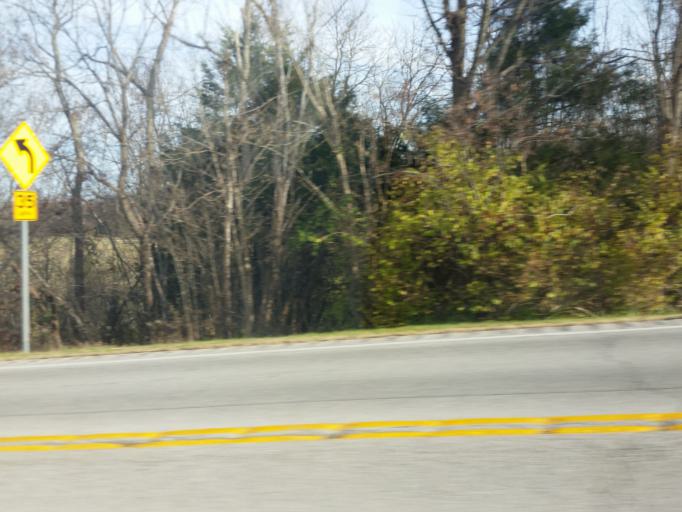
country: US
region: Kentucky
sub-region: Harrison County
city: Cynthiana
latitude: 38.4780
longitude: -84.2858
